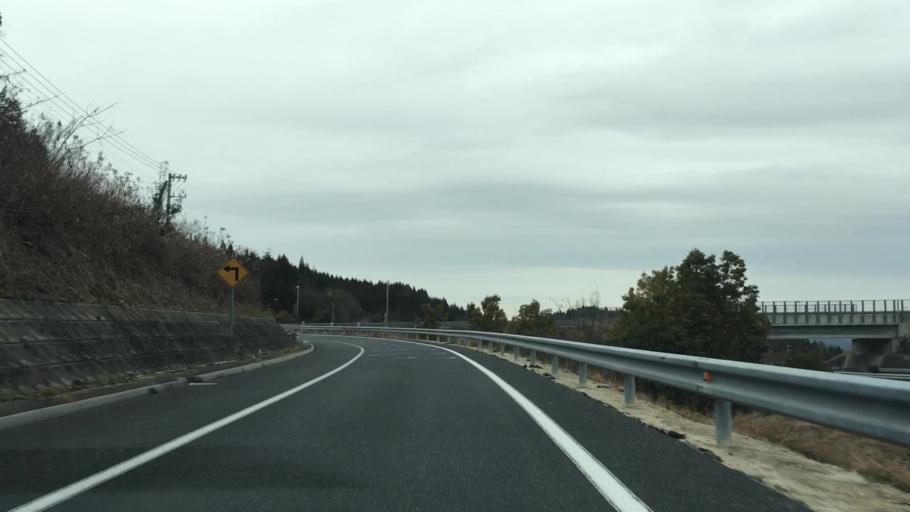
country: JP
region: Gifu
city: Toki
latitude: 35.3320
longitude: 137.1749
